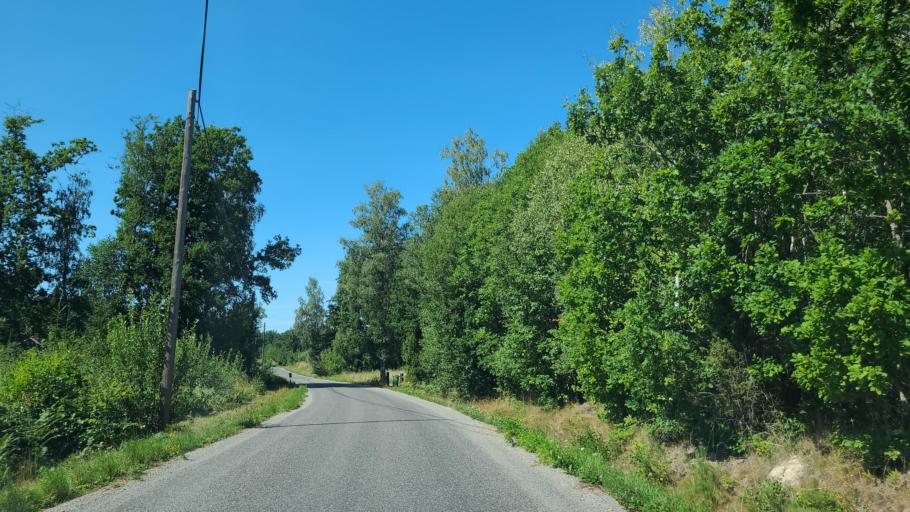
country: SE
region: Kalmar
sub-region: Kalmar Kommun
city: Ljungbyholm
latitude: 56.5704
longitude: 16.0699
